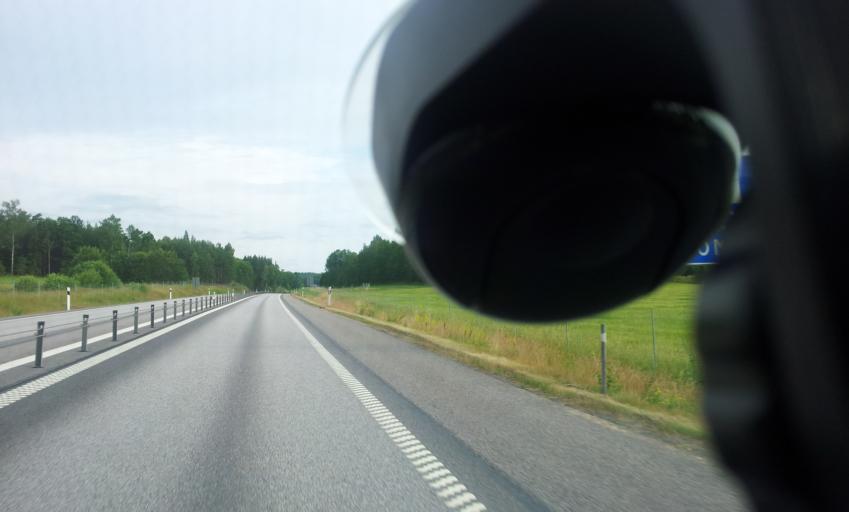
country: SE
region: OEstergoetland
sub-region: Valdemarsviks Kommun
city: Gusum
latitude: 58.3677
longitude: 16.4298
